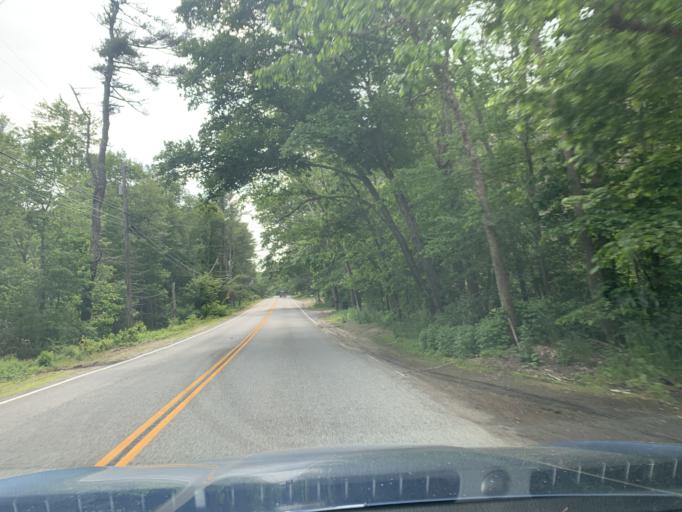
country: US
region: Rhode Island
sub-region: Kent County
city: Coventry
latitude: 41.7064
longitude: -71.7624
